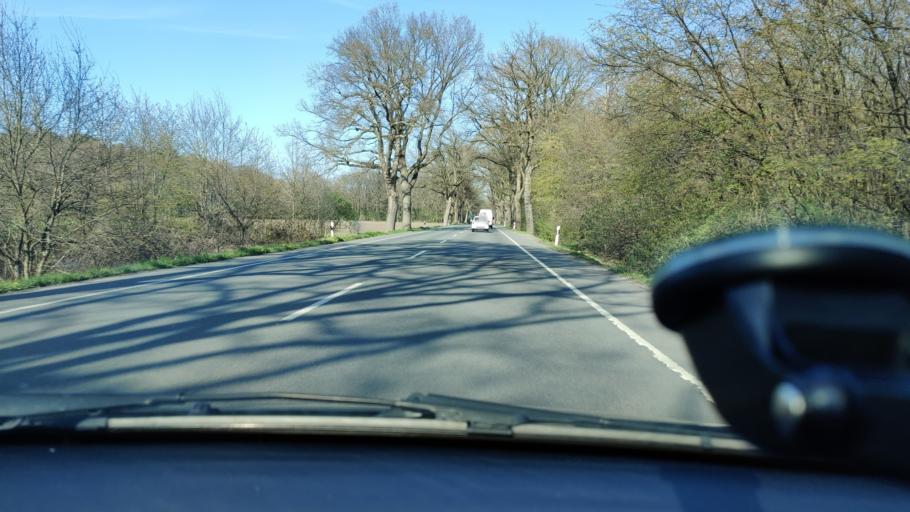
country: DE
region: North Rhine-Westphalia
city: Dorsten
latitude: 51.7172
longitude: 6.9834
